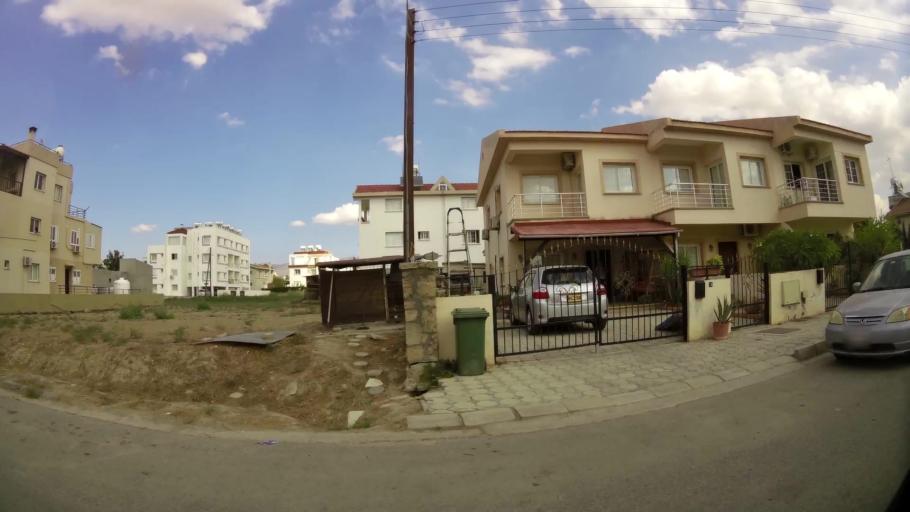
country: CY
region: Lefkosia
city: Nicosia
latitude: 35.2179
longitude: 33.2984
